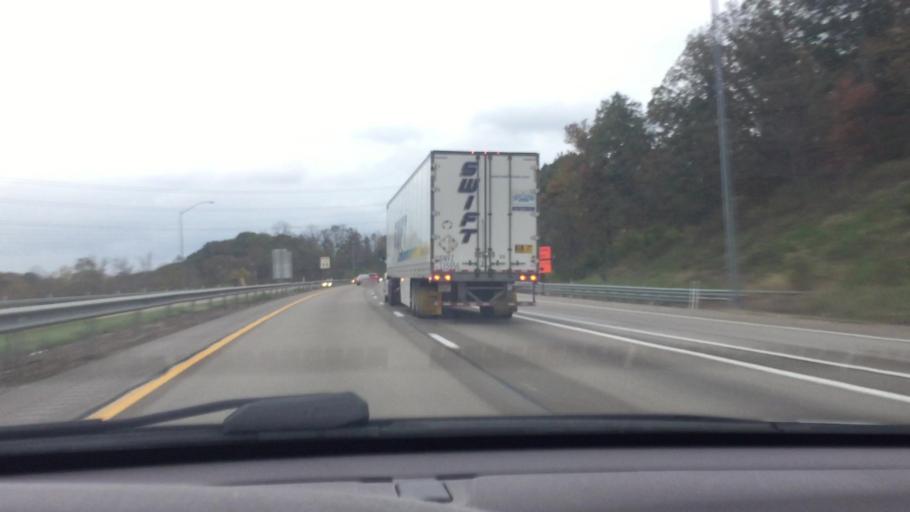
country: US
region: Pennsylvania
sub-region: Allegheny County
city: Carnegie
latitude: 40.4323
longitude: -80.1090
